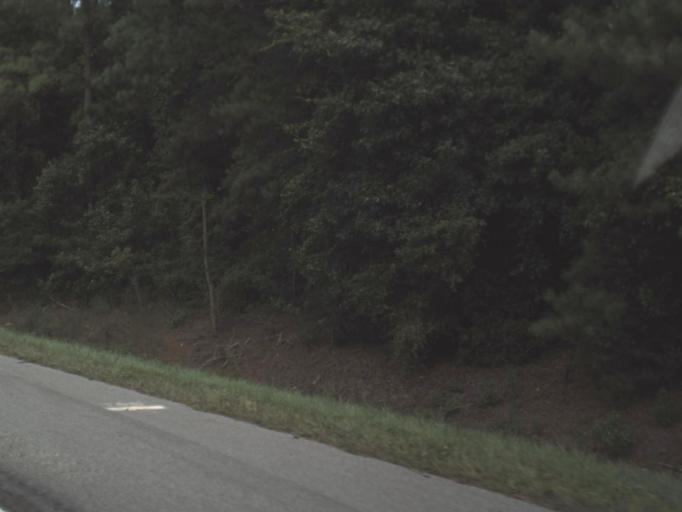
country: US
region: Florida
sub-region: Hernando County
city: Hill 'n Dale
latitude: 28.4512
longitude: -82.2758
